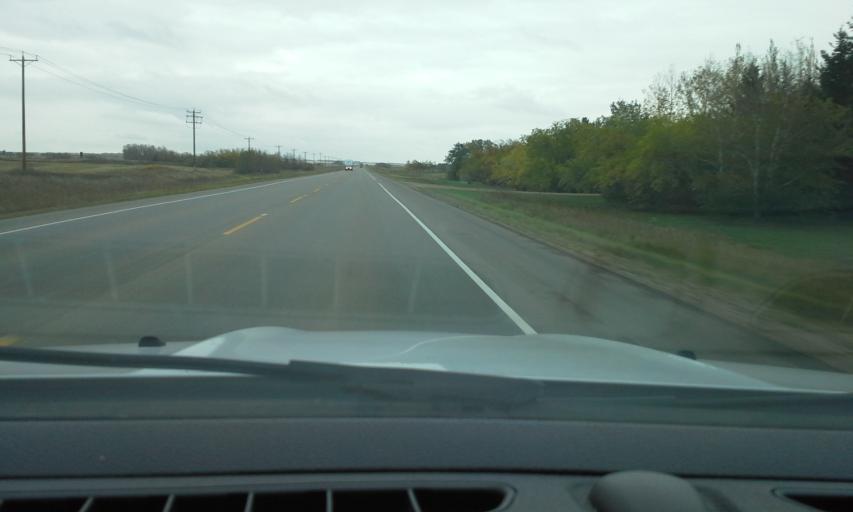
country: CA
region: Saskatchewan
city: Lloydminster
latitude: 53.2780
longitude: -109.8282
